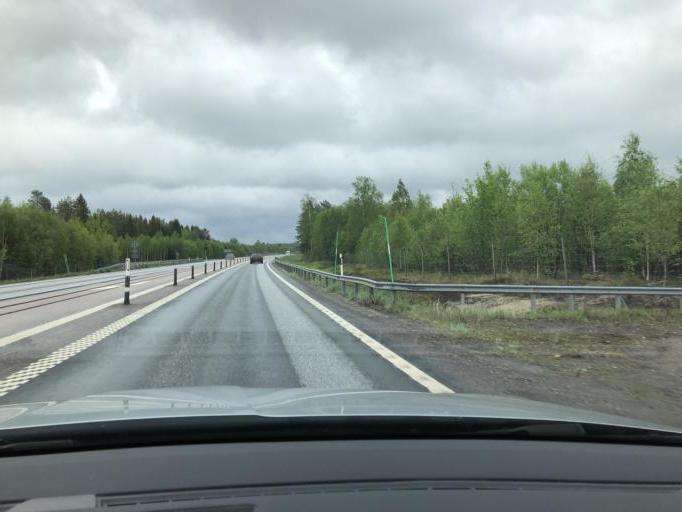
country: SE
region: Vaesterbotten
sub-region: Nordmalings Kommun
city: Nordmaling
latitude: 63.5652
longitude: 19.4311
